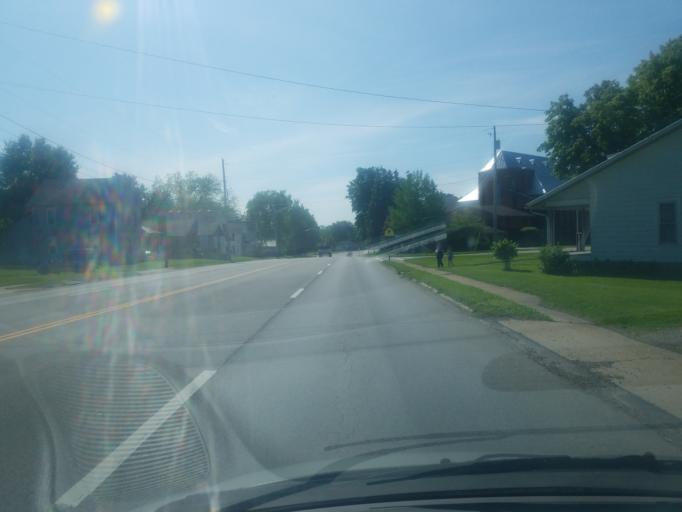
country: US
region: Ohio
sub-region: Huron County
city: Monroeville
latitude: 41.2467
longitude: -82.6982
